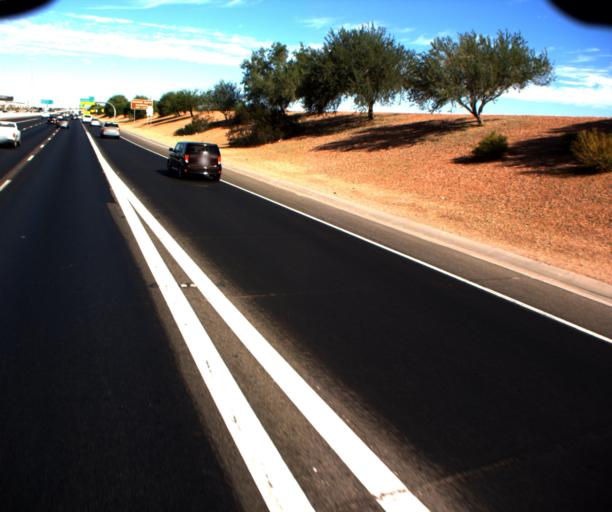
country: US
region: Arizona
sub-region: Maricopa County
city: Tolleson
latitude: 33.4980
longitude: -112.2653
